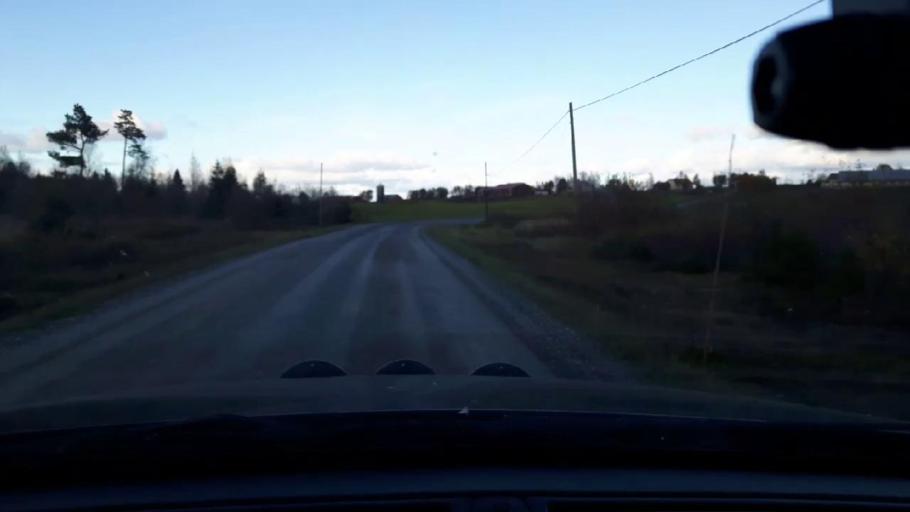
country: SE
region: Jaemtland
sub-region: Krokoms Kommun
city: Krokom
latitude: 63.0761
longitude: 14.2716
